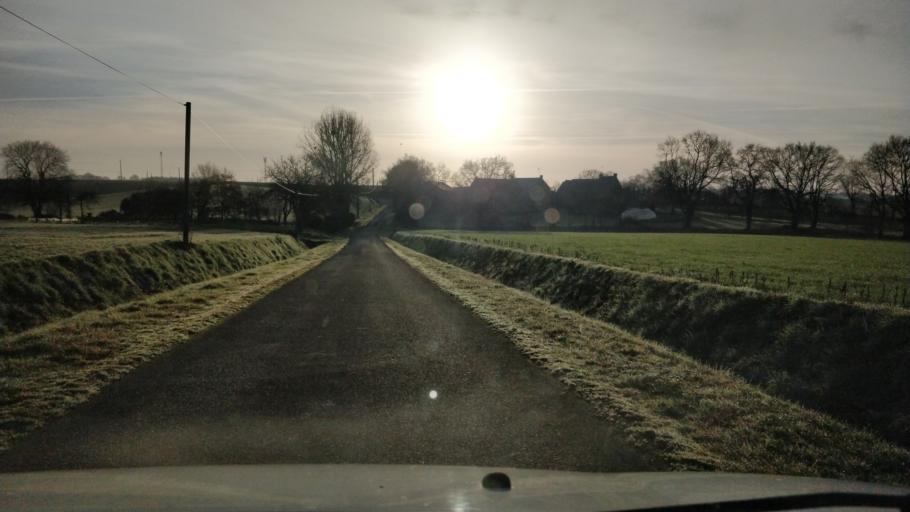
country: FR
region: Brittany
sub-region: Departement d'Ille-et-Vilaine
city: Bais
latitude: 48.0136
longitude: -1.3126
